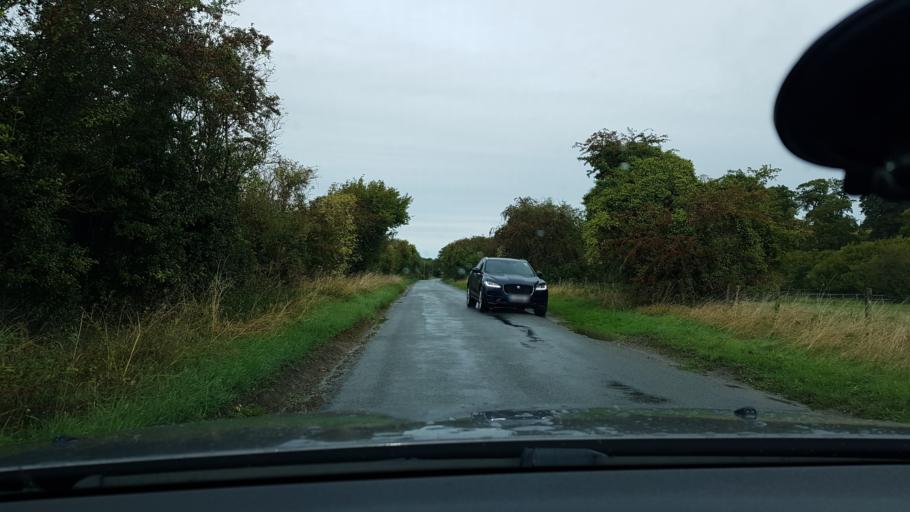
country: GB
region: England
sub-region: West Berkshire
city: Lambourn
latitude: 51.5342
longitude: -1.5277
